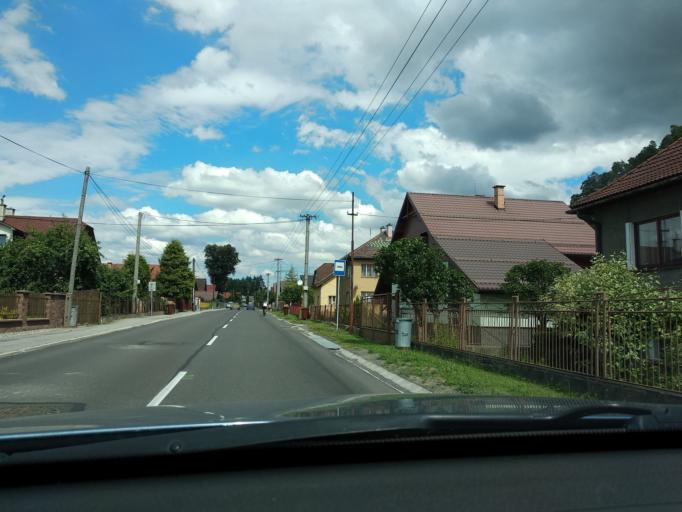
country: SK
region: Zilinsky
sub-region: Okres Zilina
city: Liptovsky Hradok
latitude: 49.0463
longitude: 19.7386
